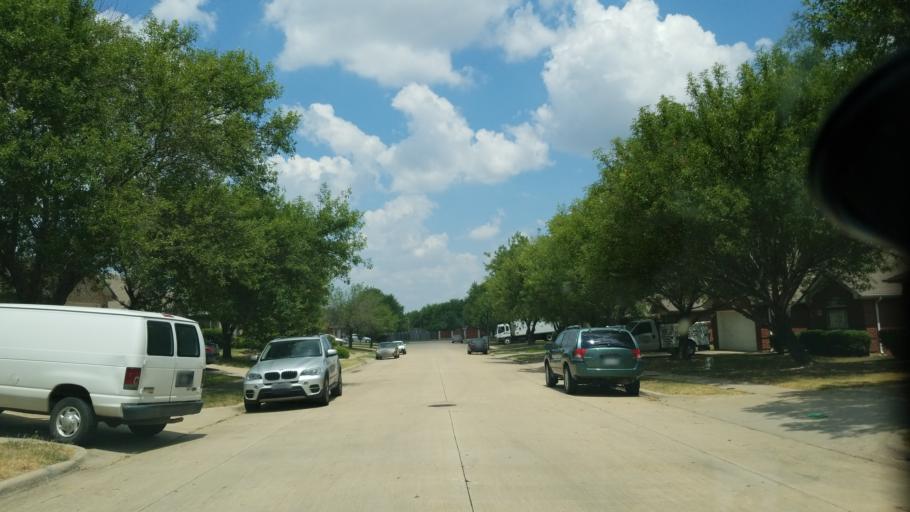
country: US
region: Texas
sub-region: Dallas County
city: Duncanville
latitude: 32.6779
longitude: -96.8968
